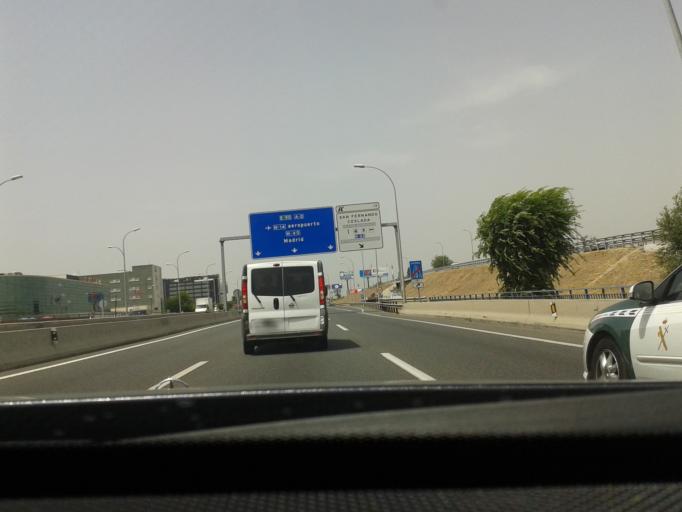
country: ES
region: Madrid
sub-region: Provincia de Madrid
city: San Fernando de Henares
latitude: 40.4477
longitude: -3.5400
